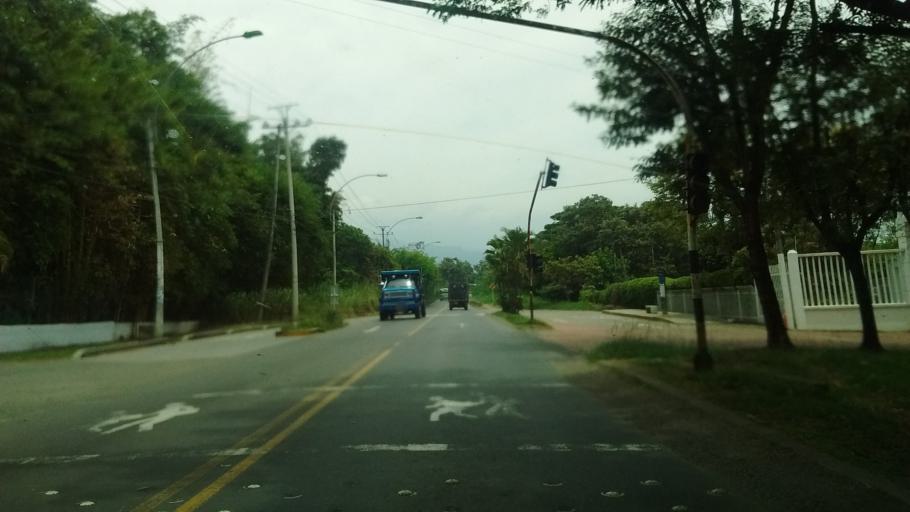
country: CO
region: Valle del Cauca
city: Jamundi
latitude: 3.3414
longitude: -76.5215
